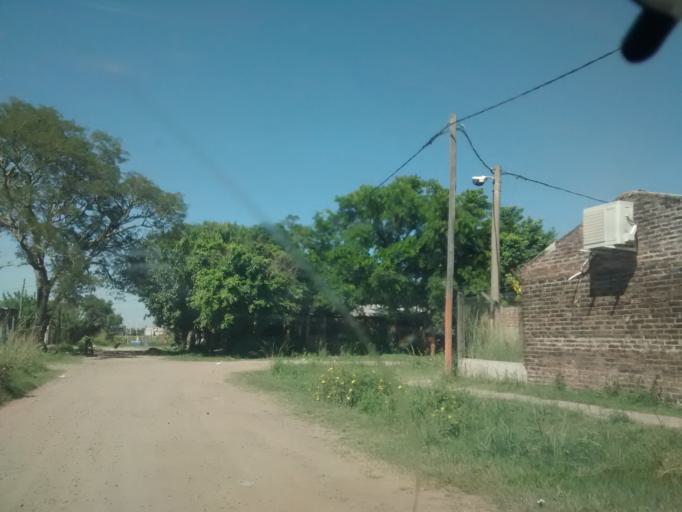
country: AR
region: Chaco
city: Fontana
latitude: -27.4096
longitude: -58.9937
